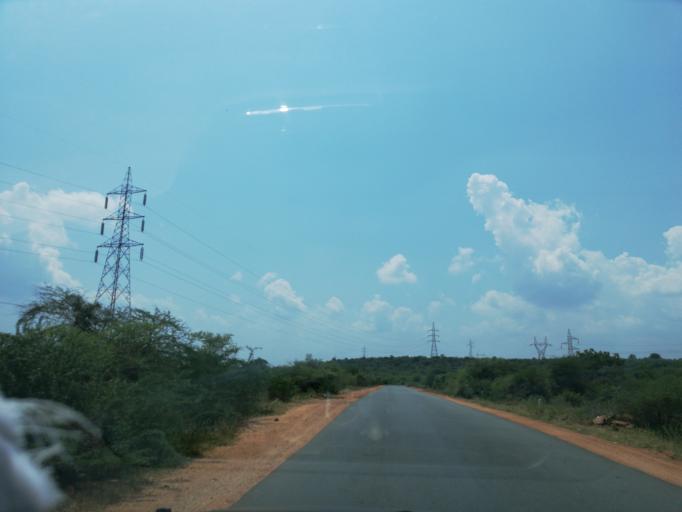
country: IN
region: Andhra Pradesh
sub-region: Guntur
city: Macherla
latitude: 16.5666
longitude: 79.3476
